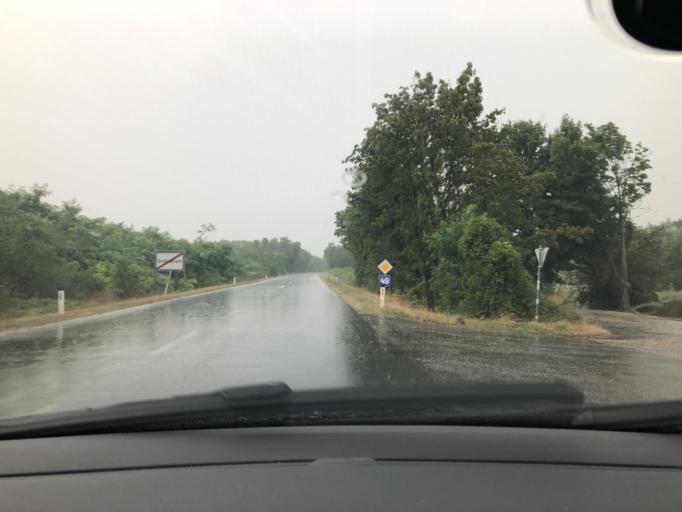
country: AT
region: Lower Austria
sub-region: Politischer Bezirk Ganserndorf
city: Marchegg
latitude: 48.2256
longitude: 16.9029
